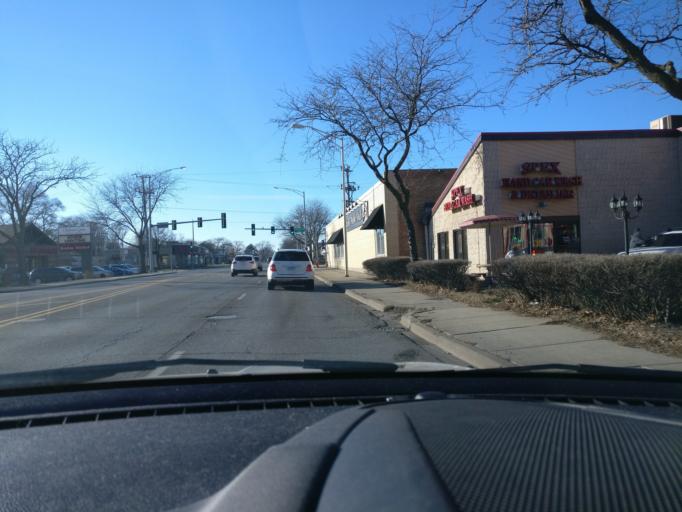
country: US
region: Illinois
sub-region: Cook County
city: Skokie
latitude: 42.0409
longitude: -87.7190
